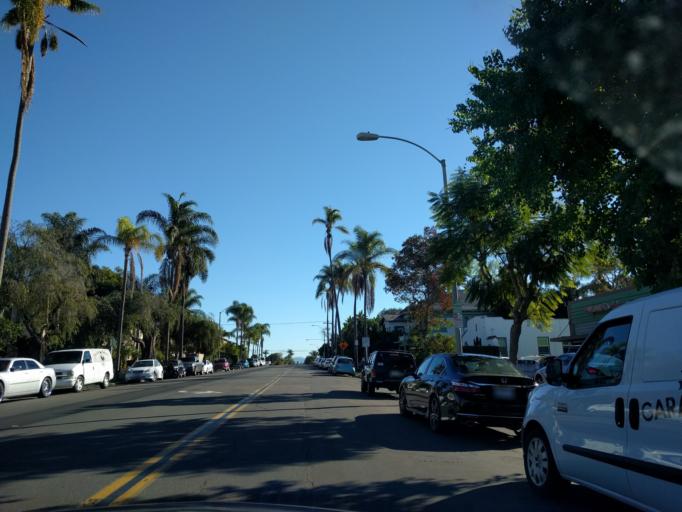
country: US
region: California
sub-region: San Diego County
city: San Diego
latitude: 32.7168
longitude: -117.1401
